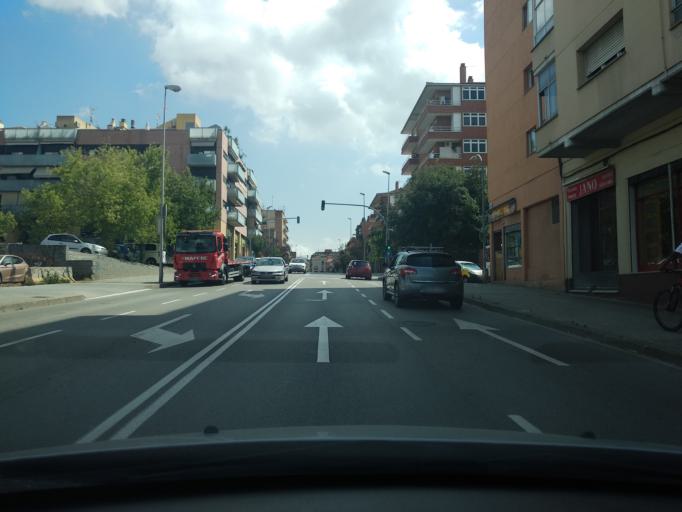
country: ES
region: Catalonia
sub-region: Provincia de Barcelona
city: Canovelles
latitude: 41.6141
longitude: 2.2869
